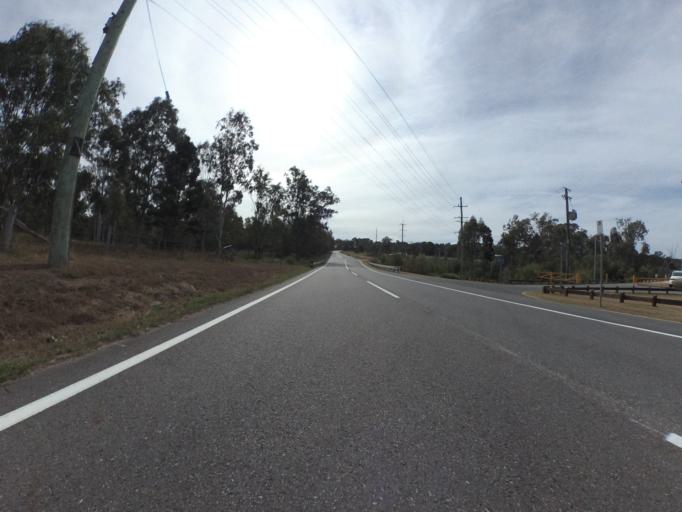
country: AU
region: Queensland
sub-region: Brisbane
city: Moggill
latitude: -27.5808
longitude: 152.8622
